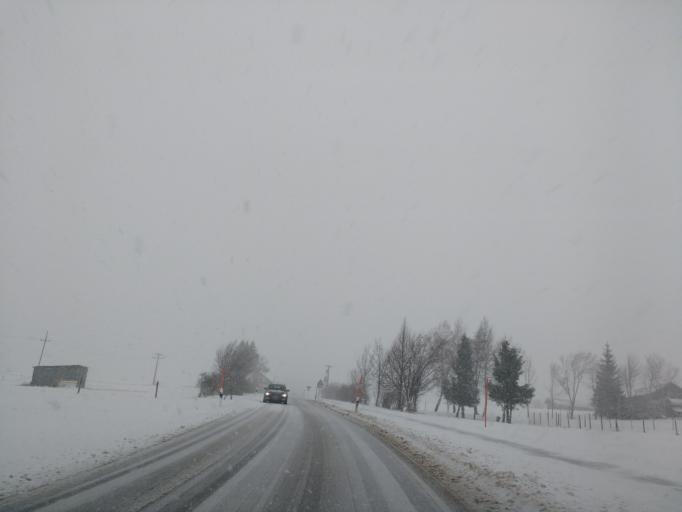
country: DE
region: Bavaria
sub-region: Swabia
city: Buchenberg
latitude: 47.7047
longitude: 10.2214
